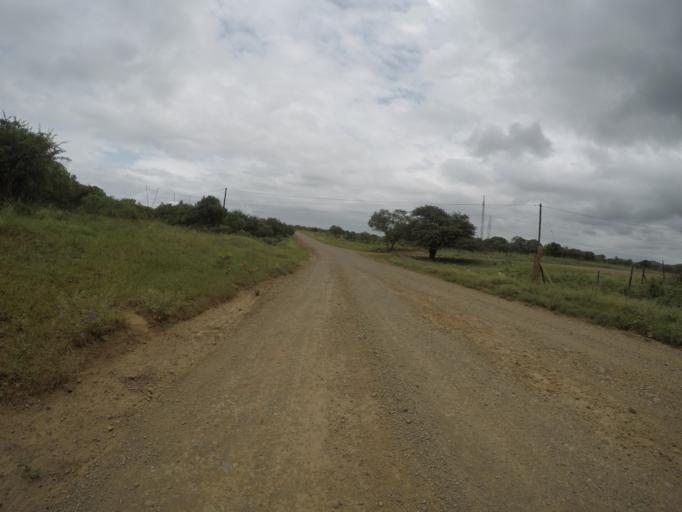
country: ZA
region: KwaZulu-Natal
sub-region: uThungulu District Municipality
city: Empangeni
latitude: -28.6013
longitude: 31.8274
